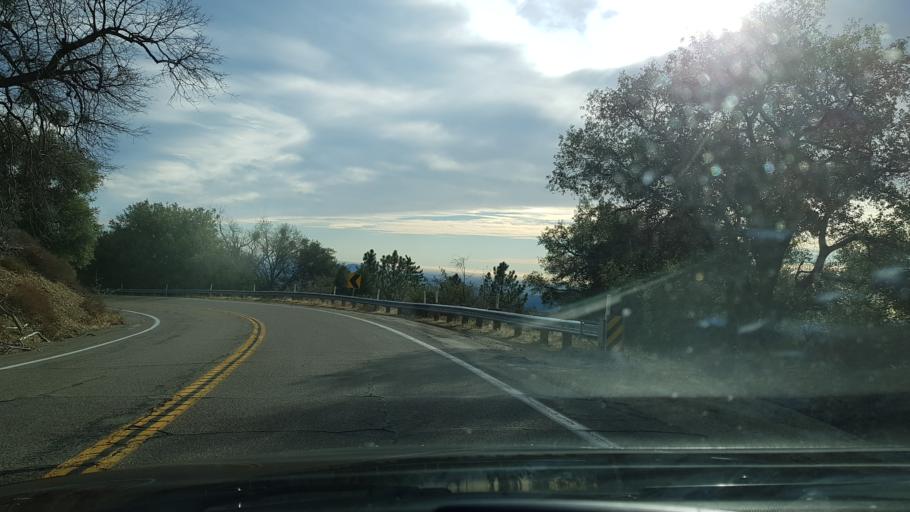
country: US
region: California
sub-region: Riverside County
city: Aguanga
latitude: 33.3087
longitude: -116.8726
